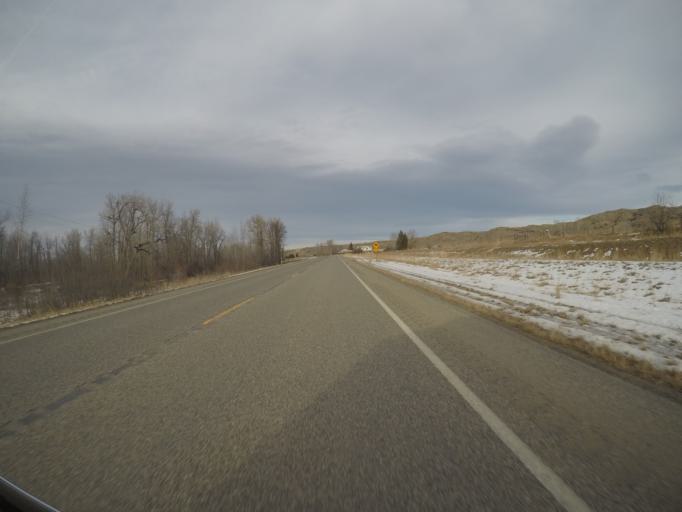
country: US
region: Montana
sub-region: Stillwater County
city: Absarokee
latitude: 45.4639
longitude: -109.4482
